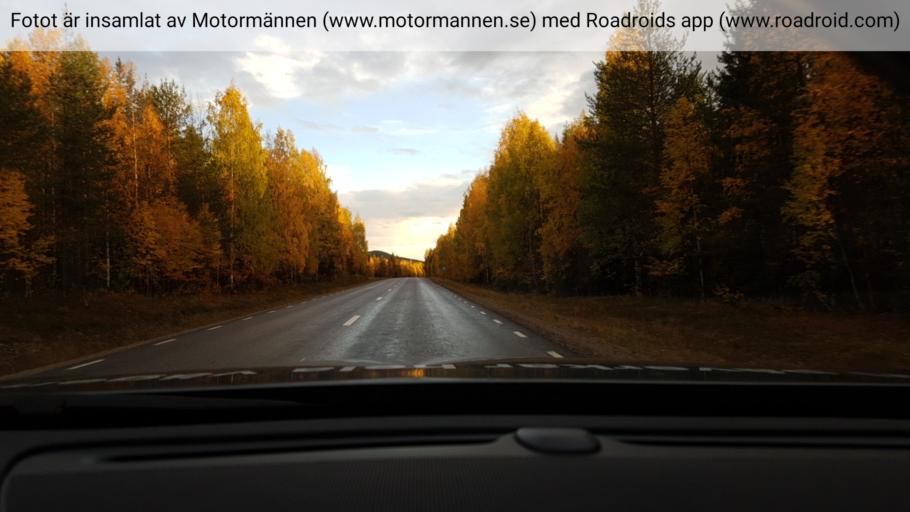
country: SE
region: Norrbotten
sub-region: Overkalix Kommun
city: OEverkalix
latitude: 66.5845
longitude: 22.7570
